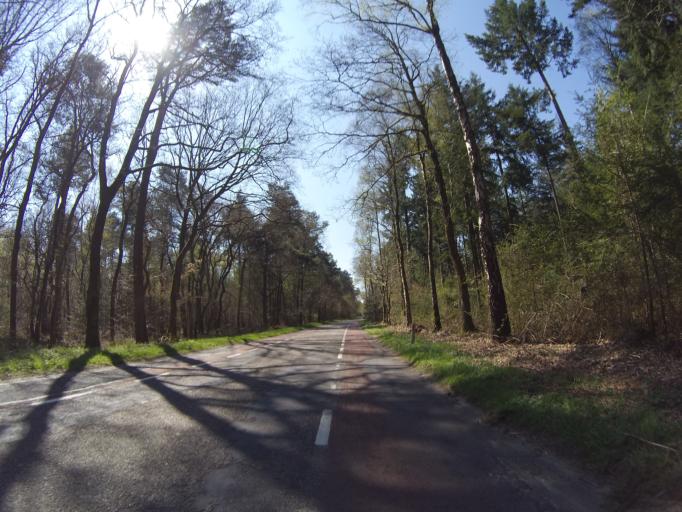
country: NL
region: Utrecht
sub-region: Gemeente Utrechtse Heuvelrug
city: Overberg
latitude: 52.0284
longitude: 5.4857
